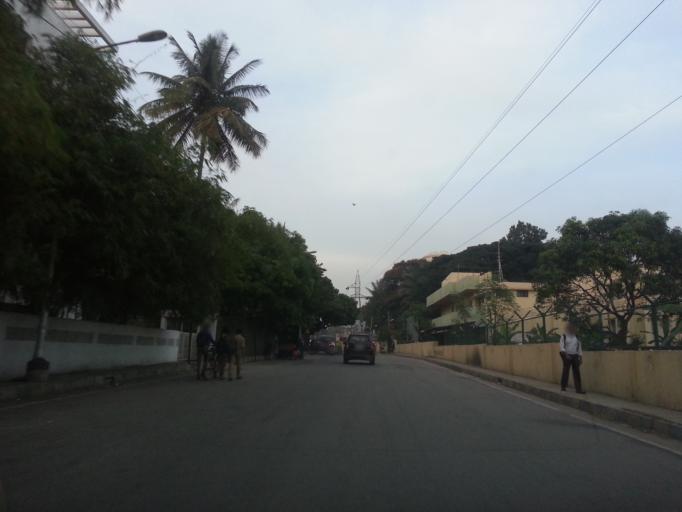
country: IN
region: Karnataka
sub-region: Bangalore Urban
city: Bangalore
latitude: 13.0024
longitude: 77.6191
